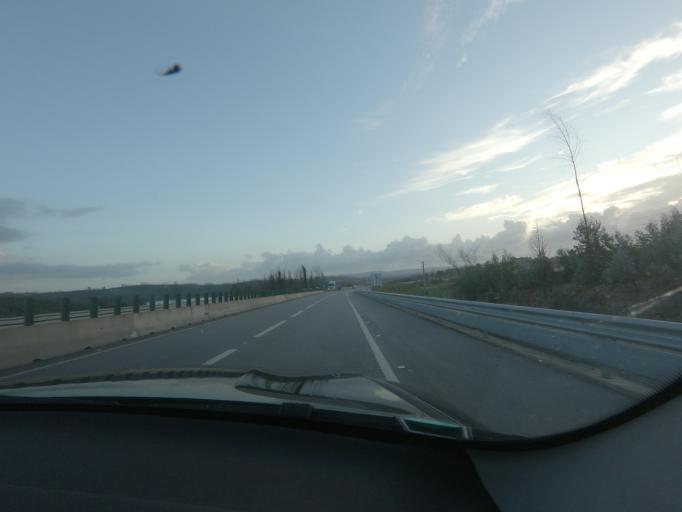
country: PT
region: Viseu
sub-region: Santa Comba Dao
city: Santa Comba Dao
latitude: 40.3481
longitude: -8.1748
